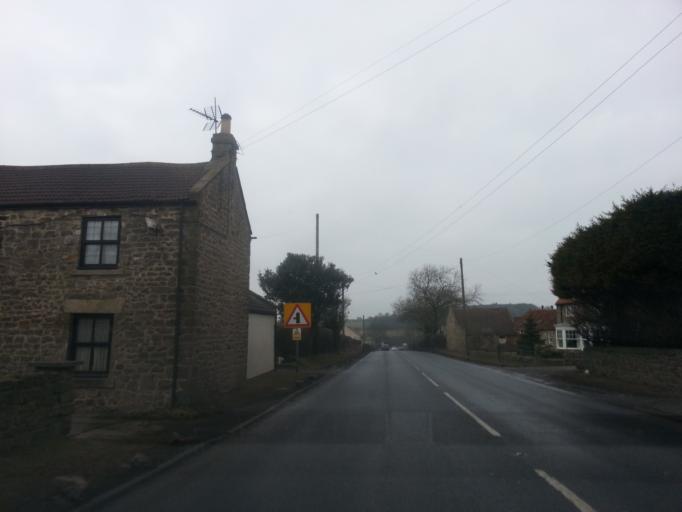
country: GB
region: England
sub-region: Darlington
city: Denton
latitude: 54.5969
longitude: -1.6613
